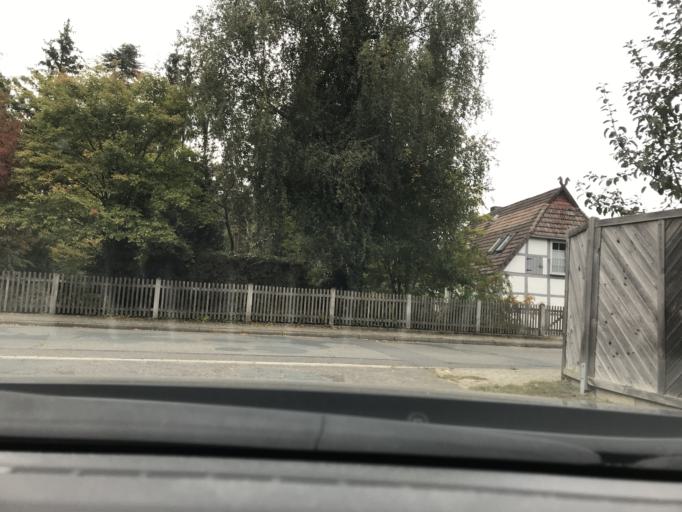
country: DE
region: Lower Saxony
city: Suderburg
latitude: 52.8930
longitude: 10.4624
